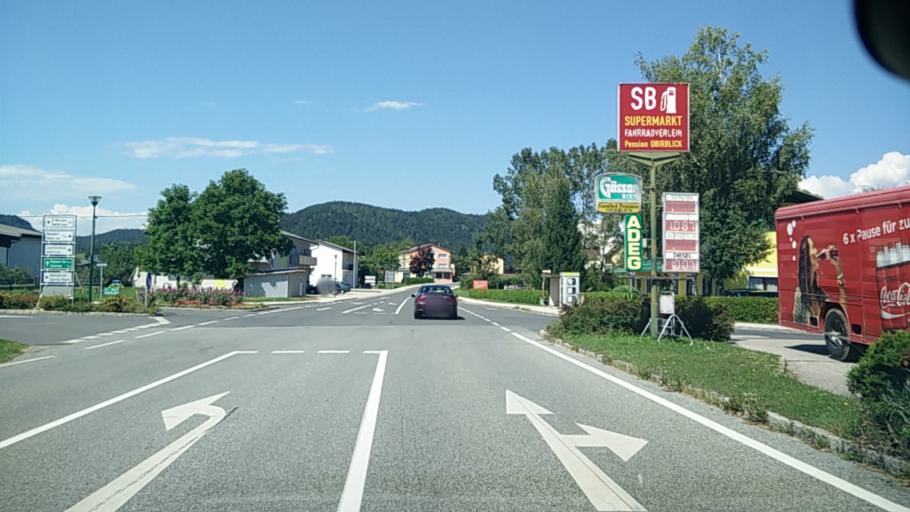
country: AT
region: Carinthia
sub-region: Politischer Bezirk Volkermarkt
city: Sittersdorf
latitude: 46.5768
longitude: 14.5644
